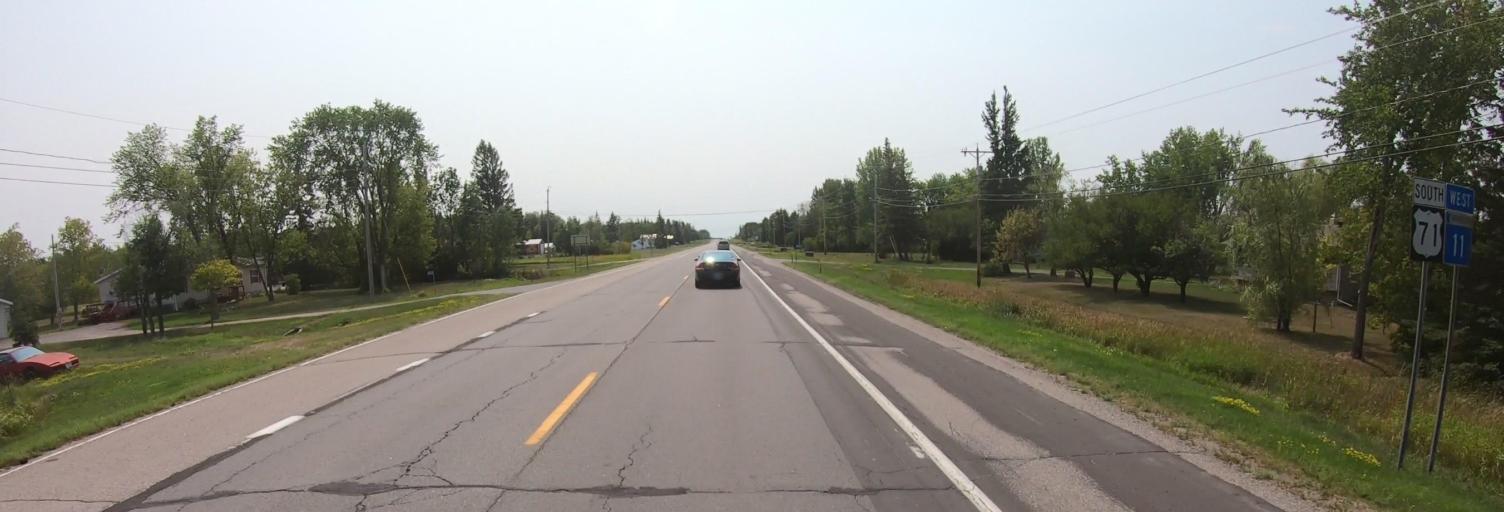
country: US
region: Minnesota
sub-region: Koochiching County
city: International Falls
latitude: 48.5765
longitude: -93.4402
